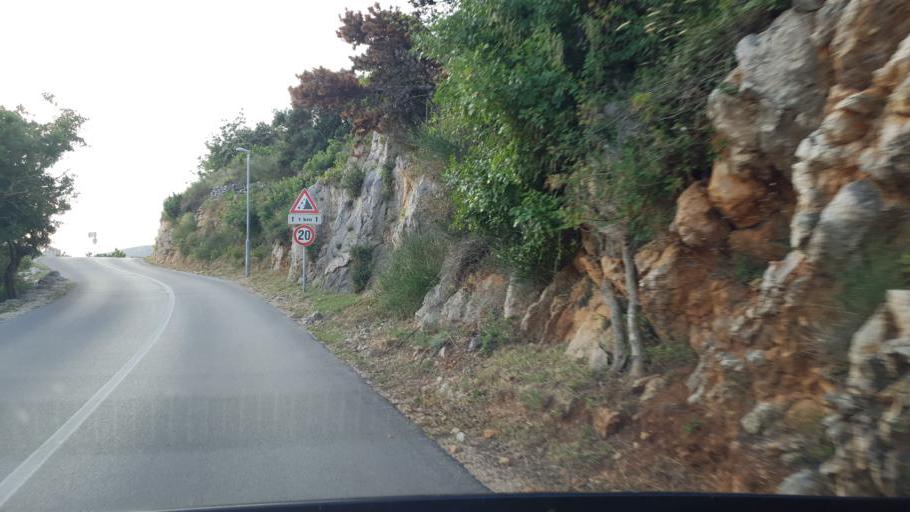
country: HR
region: Primorsko-Goranska
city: Punat
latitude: 44.9622
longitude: 14.6828
